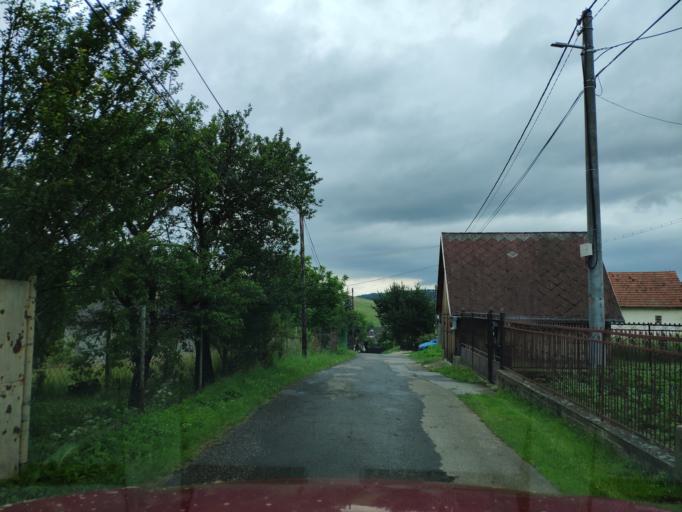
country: SK
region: Presovsky
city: Sabinov
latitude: 49.0426
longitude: 21.0160
